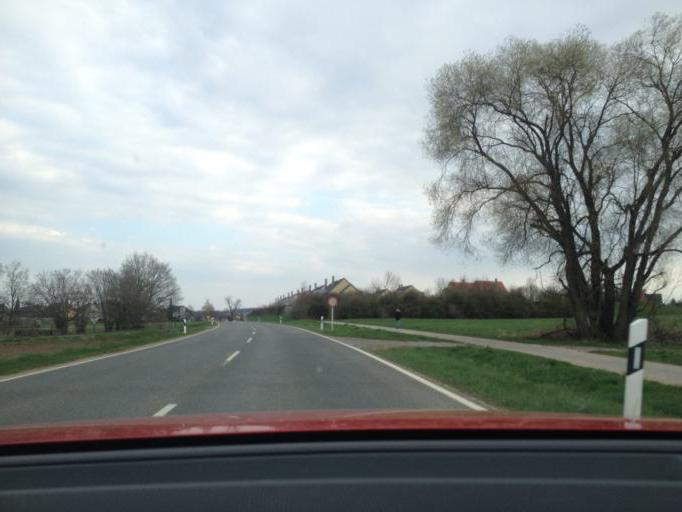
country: DE
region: Bavaria
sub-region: Upper Palatinate
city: Speinshart
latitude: 49.7599
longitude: 11.8262
